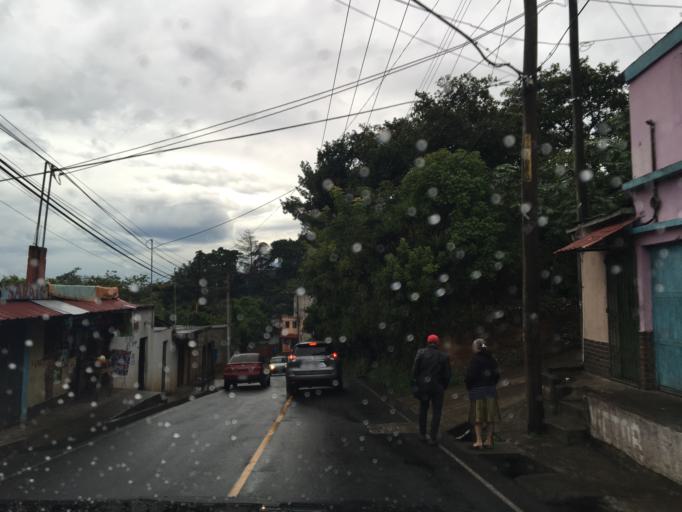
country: GT
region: Guatemala
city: Santa Catarina Pinula
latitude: 14.5463
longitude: -90.5115
